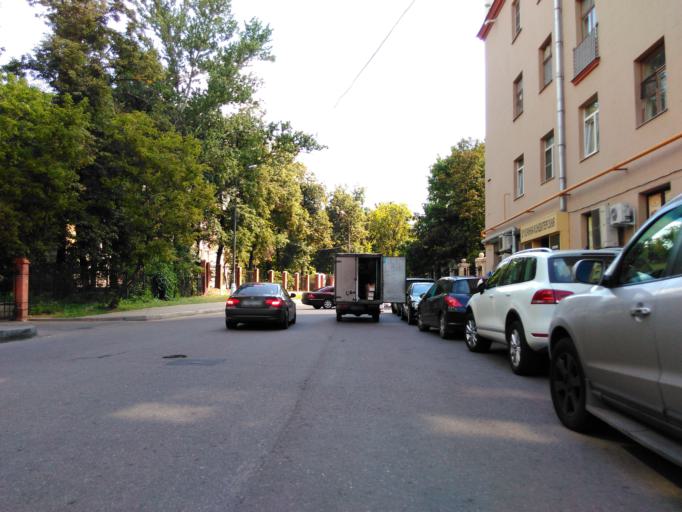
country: RU
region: Moscow
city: Novyye Cheremushki
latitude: 55.7111
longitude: 37.5868
